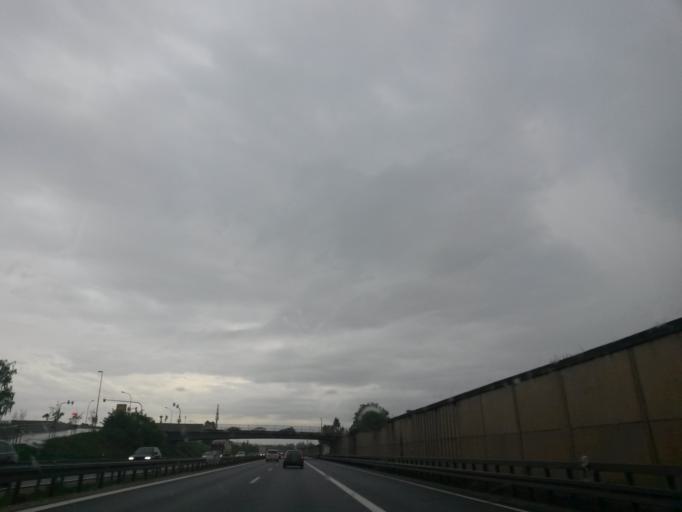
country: DE
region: Bavaria
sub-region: Regierungsbezirk Mittelfranken
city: Baiersdorf
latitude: 49.6595
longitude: 11.0378
